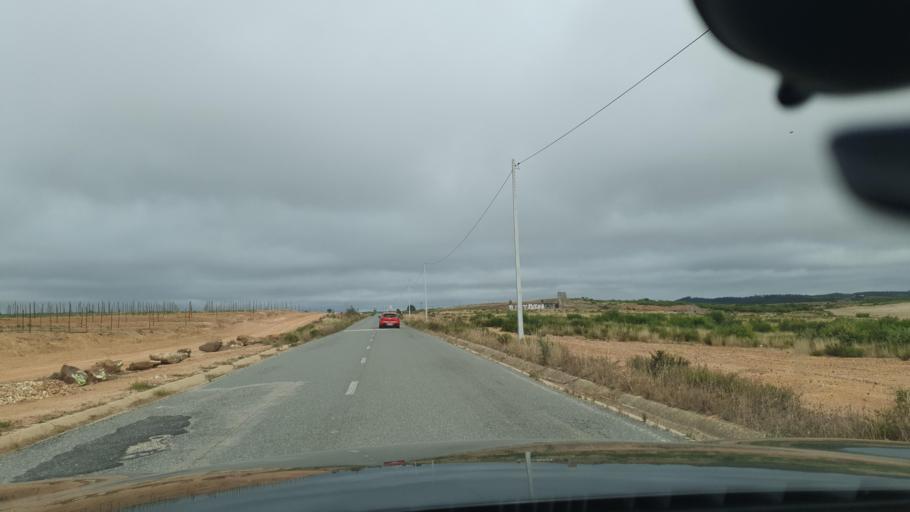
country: PT
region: Beja
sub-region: Odemira
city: Sao Teotonio
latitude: 37.5487
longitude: -8.7401
